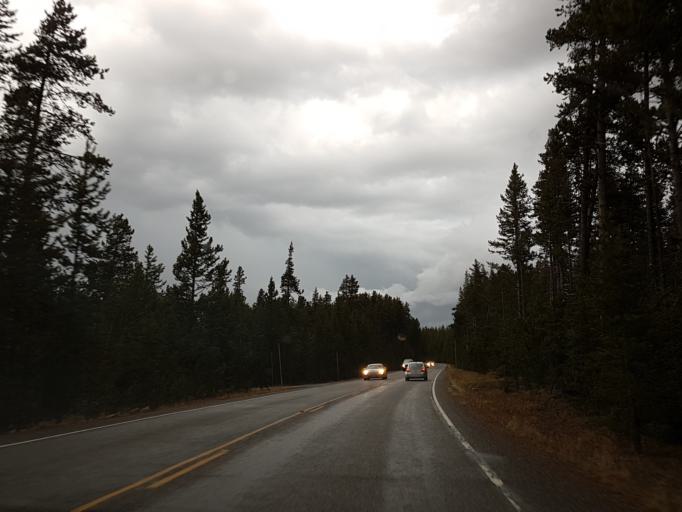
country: US
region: Montana
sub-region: Gallatin County
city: West Yellowstone
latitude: 44.4560
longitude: -110.5080
